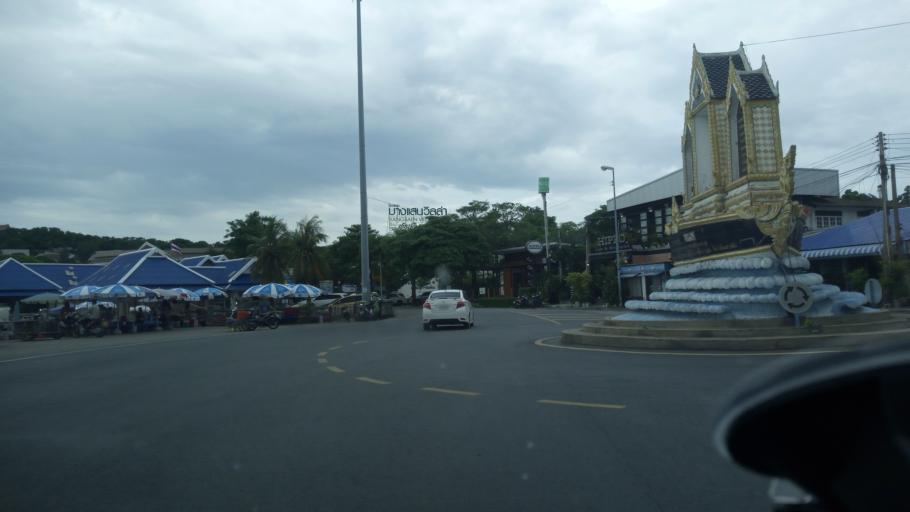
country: TH
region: Chon Buri
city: Chon Buri
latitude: 13.3037
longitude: 100.9020
